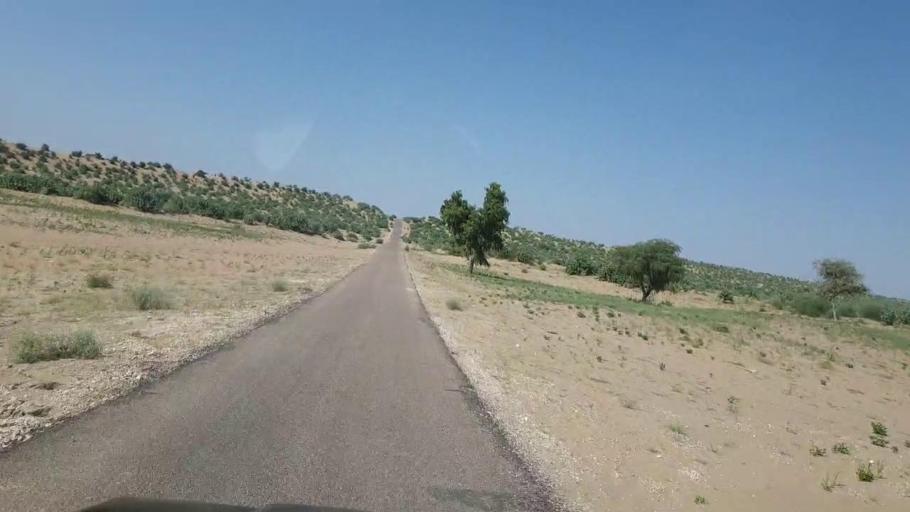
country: PK
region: Sindh
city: Chor
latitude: 25.6168
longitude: 70.3177
